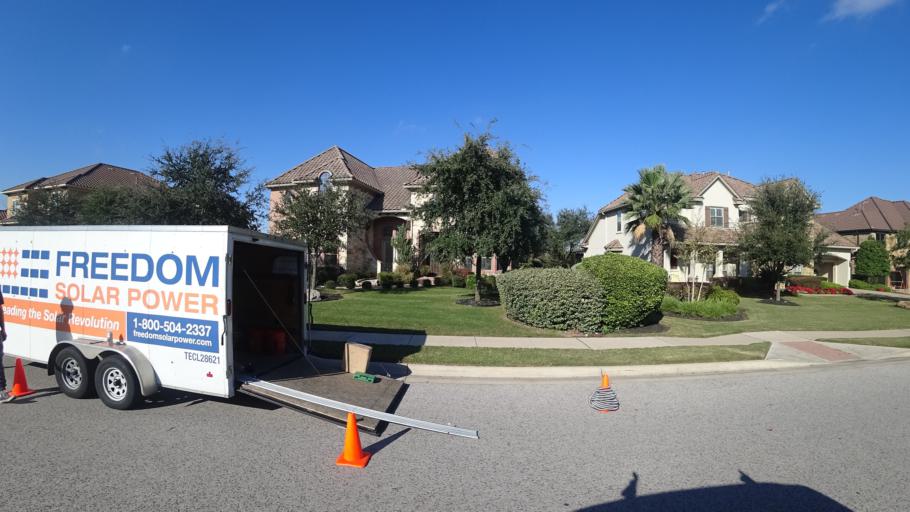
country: US
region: Texas
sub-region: Travis County
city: Bee Cave
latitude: 30.3542
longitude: -97.8930
